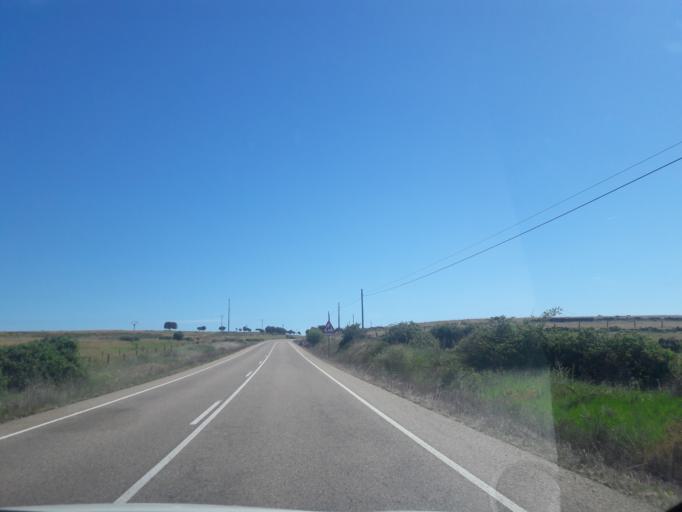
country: ES
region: Castille and Leon
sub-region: Provincia de Salamanca
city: Cerralbo
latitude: 40.9779
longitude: -6.5780
